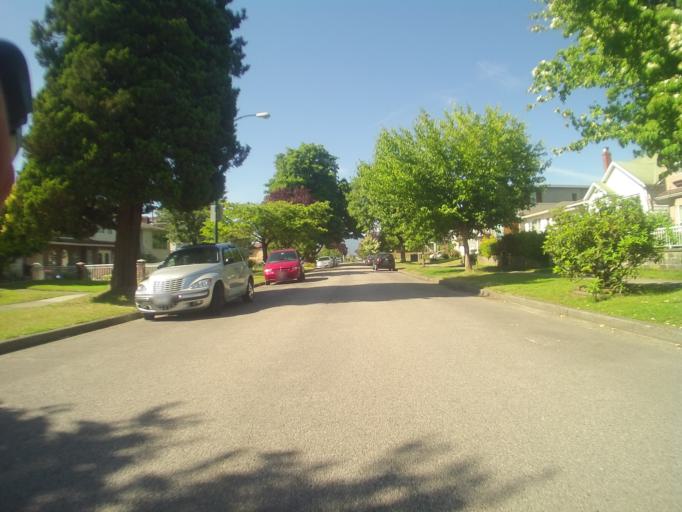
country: CA
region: British Columbia
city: Vancouver
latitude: 49.2341
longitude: -123.0797
